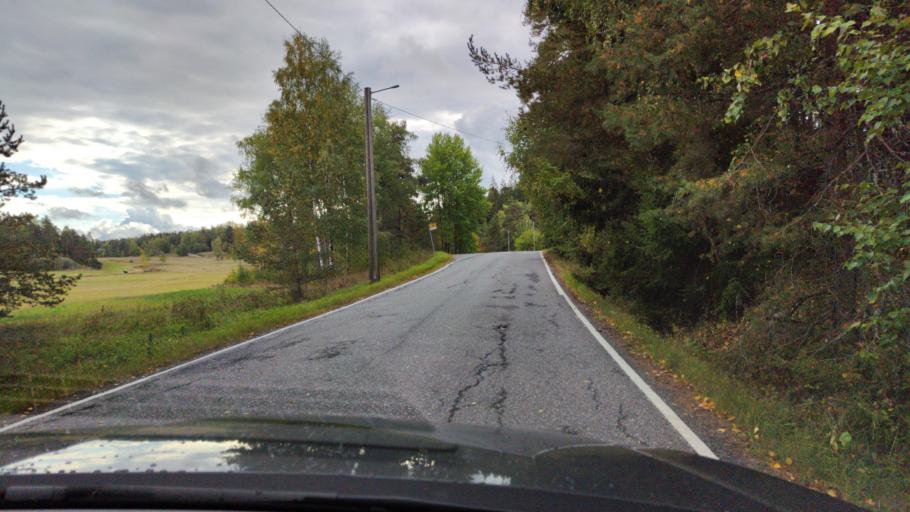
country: FI
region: Varsinais-Suomi
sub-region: Aboland-Turunmaa
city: Pargas
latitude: 60.3703
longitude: 22.2768
